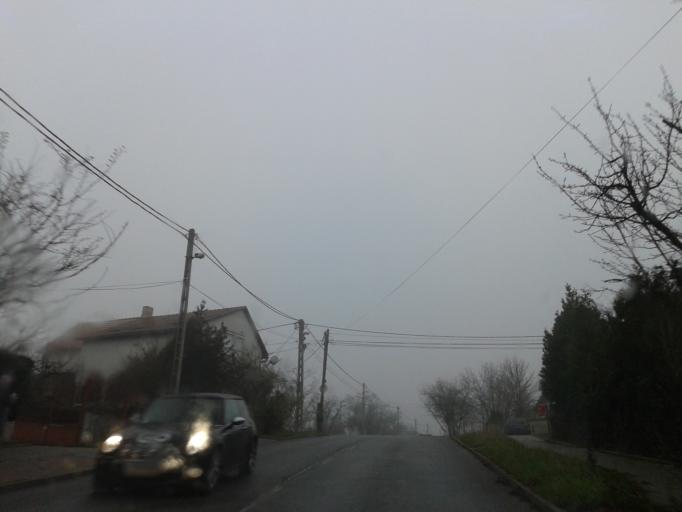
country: HU
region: Budapest
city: Budapest XXII. keruelet
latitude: 47.4375
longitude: 19.0136
